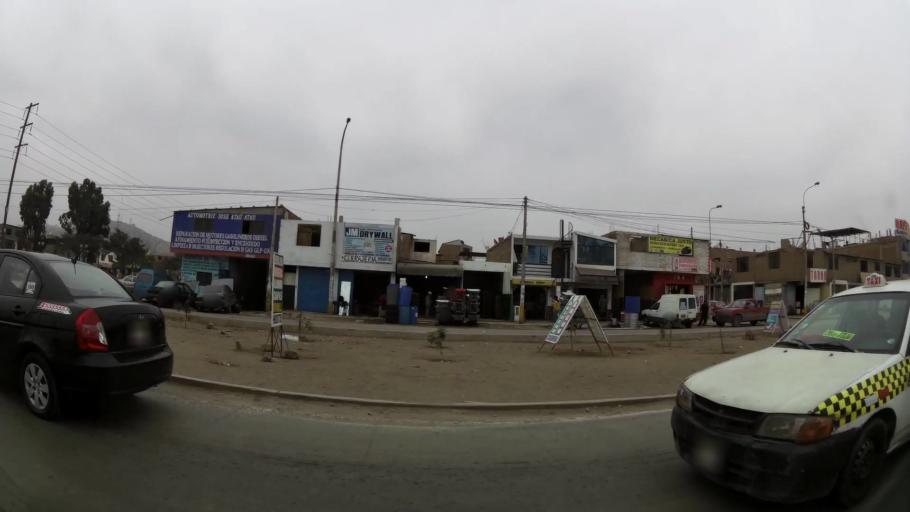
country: PE
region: Lima
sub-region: Lima
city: Surco
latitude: -12.1985
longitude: -76.9573
